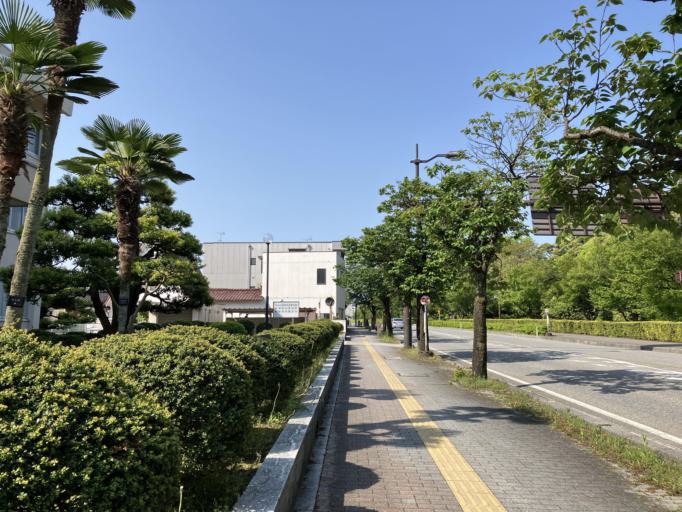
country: JP
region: Toyama
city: Takaoka
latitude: 36.7488
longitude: 137.0248
